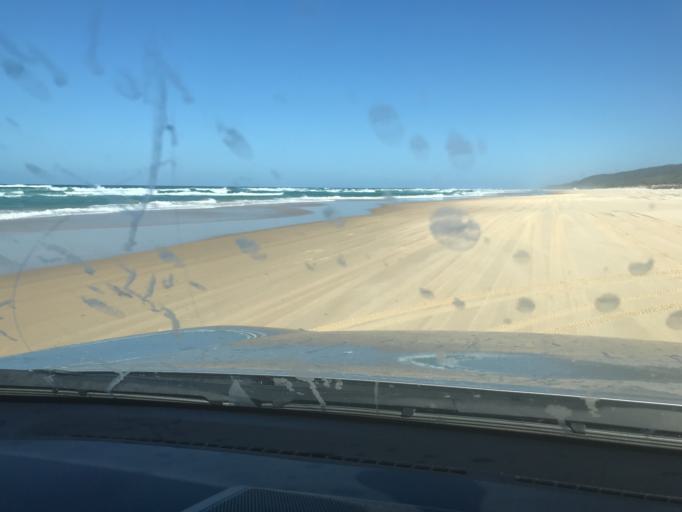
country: AU
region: Queensland
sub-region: Fraser Coast
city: Urangan
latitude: -25.0320
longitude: 153.3509
